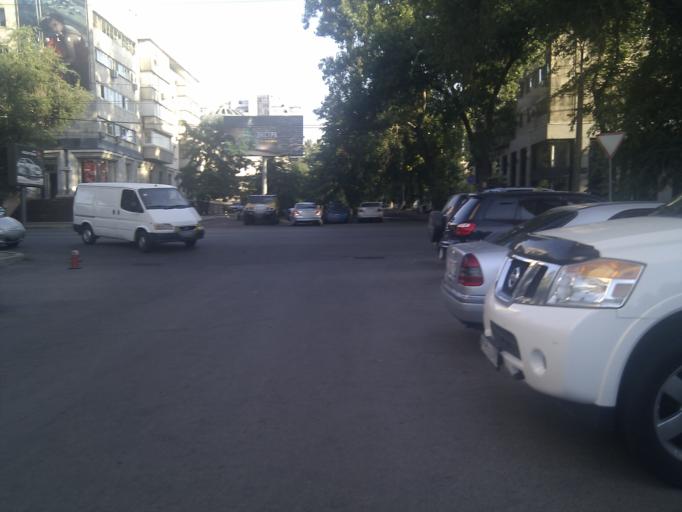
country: KZ
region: Almaty Qalasy
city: Almaty
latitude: 43.2603
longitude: 76.9477
